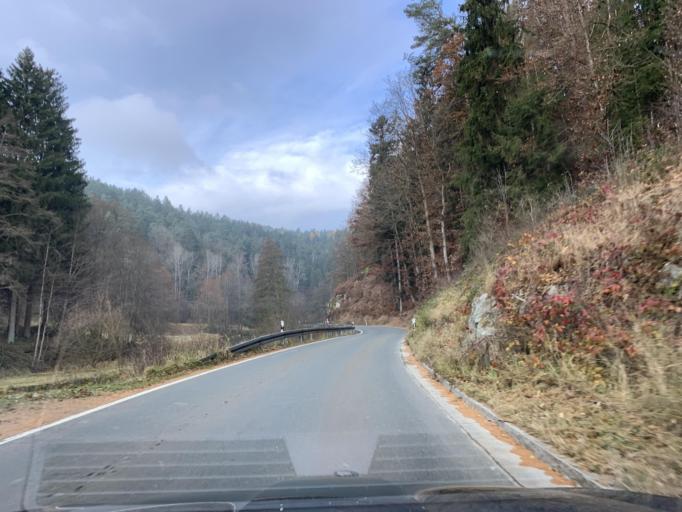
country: DE
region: Bavaria
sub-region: Upper Palatinate
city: Thanstein
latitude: 49.3638
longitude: 12.4346
